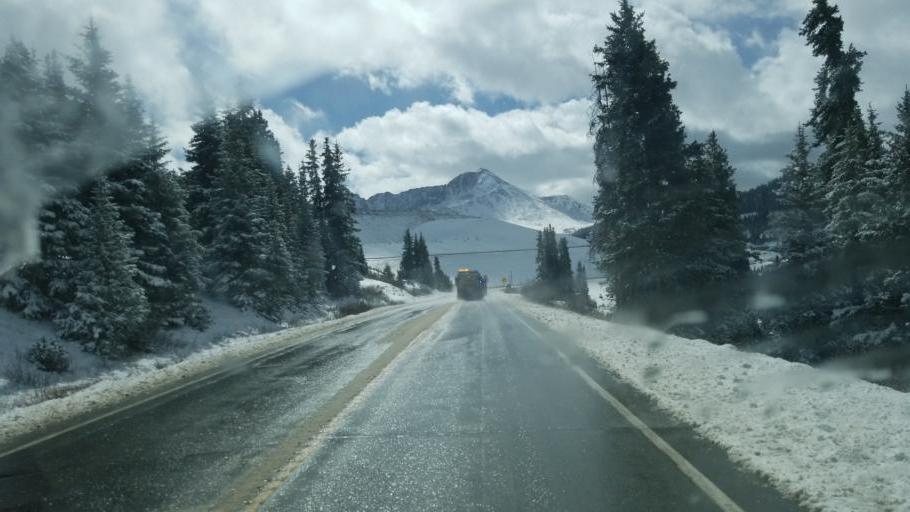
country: US
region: Colorado
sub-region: Lake County
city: Leadville
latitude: 39.3855
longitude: -106.1912
